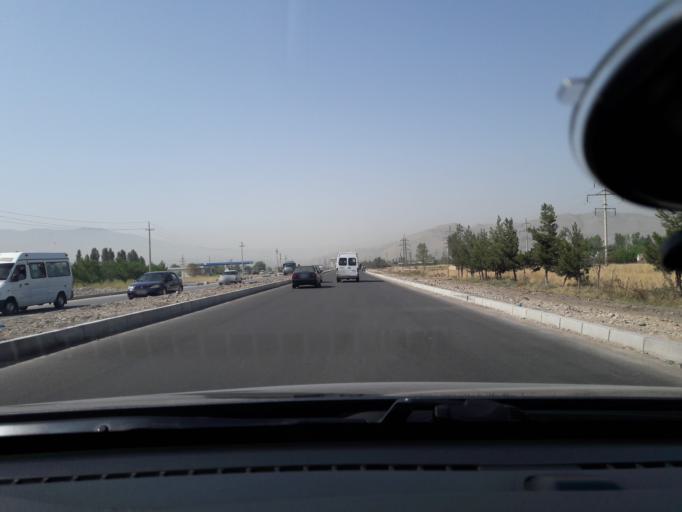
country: TJ
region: Dushanbe
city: Boshkengash
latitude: 38.4792
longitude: 68.7458
